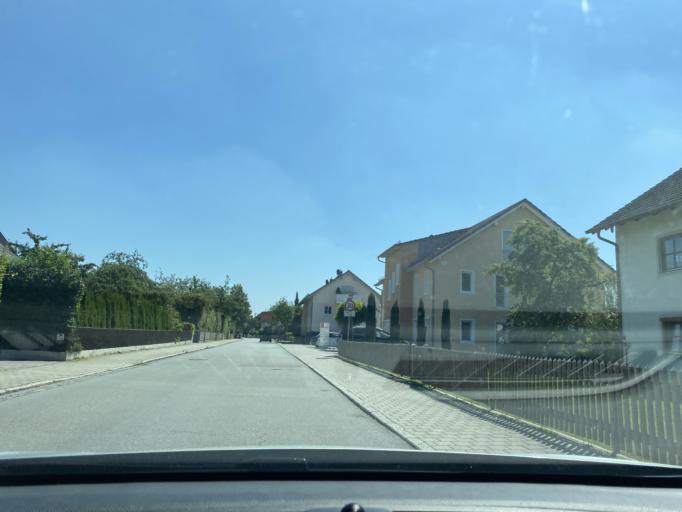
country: DE
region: Bavaria
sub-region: Upper Bavaria
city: Moosinning
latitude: 48.2748
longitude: 11.8389
